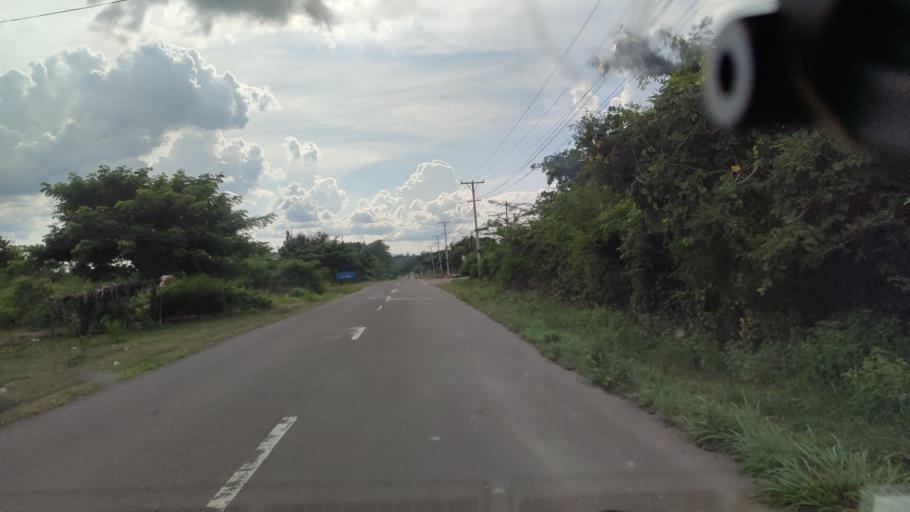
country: MM
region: Mandalay
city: Meiktila
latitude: 20.8162
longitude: 95.3983
